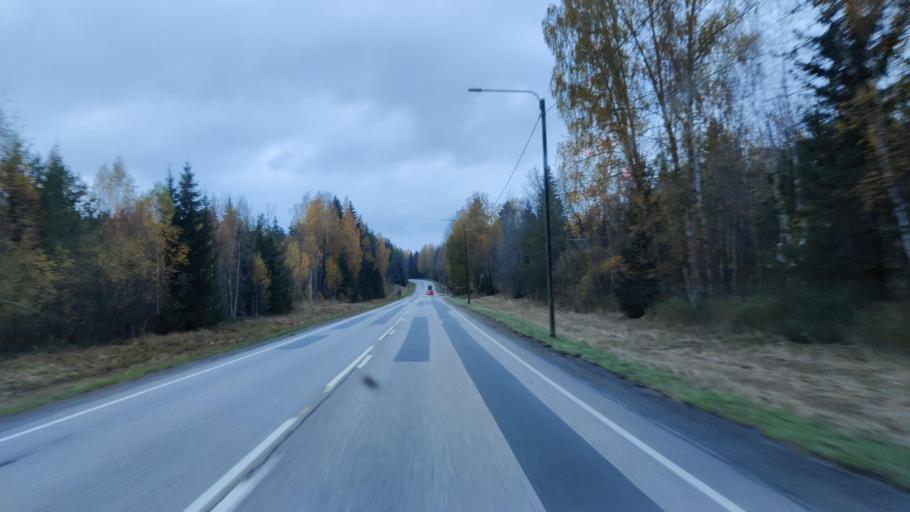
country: FI
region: Uusimaa
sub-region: Helsinki
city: Vihti
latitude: 60.3300
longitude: 24.2113
